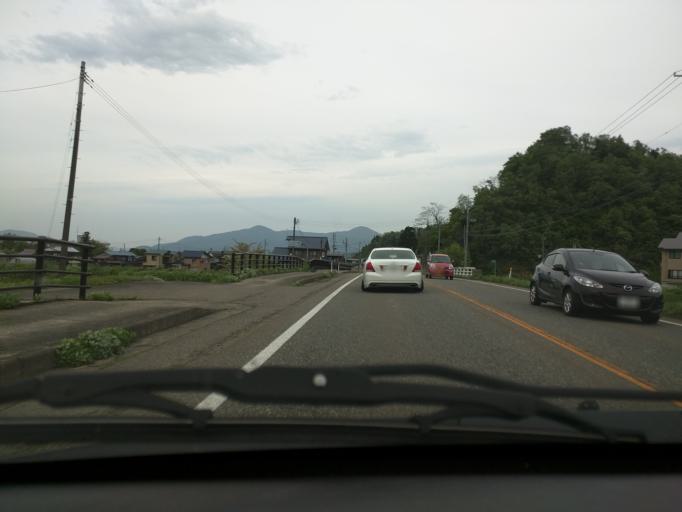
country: JP
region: Niigata
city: Muikamachi
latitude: 37.1959
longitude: 138.9494
